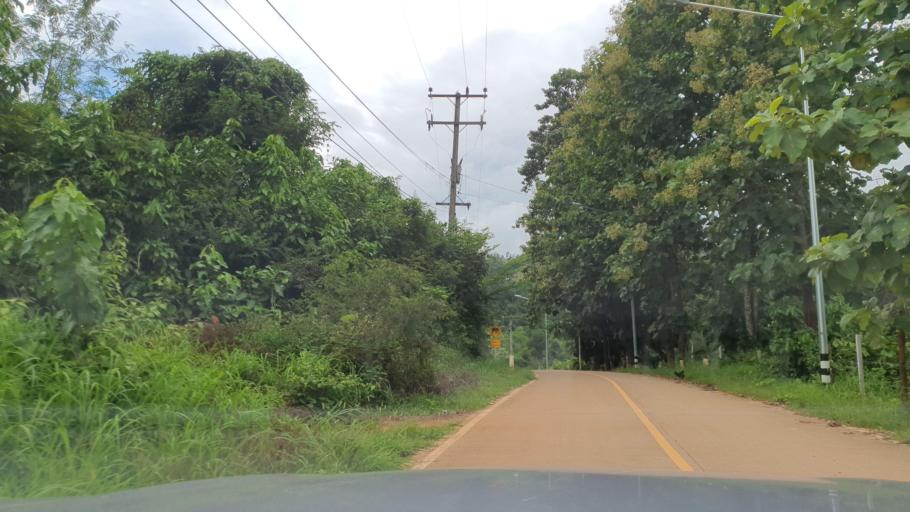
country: TH
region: Chiang Mai
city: Mae Wang
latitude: 18.6669
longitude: 98.6255
